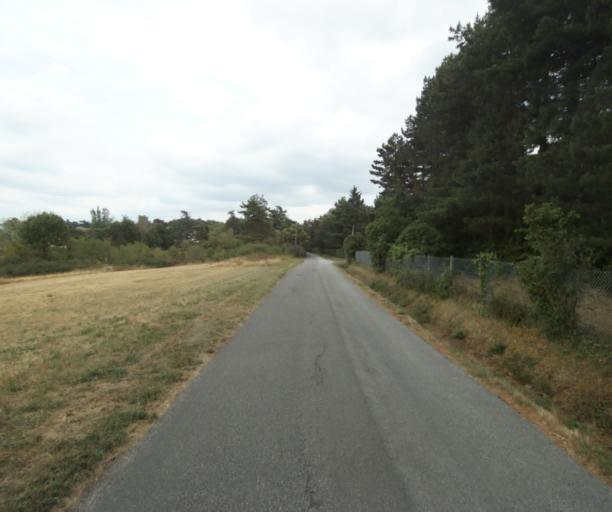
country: FR
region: Midi-Pyrenees
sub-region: Departement de la Haute-Garonne
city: Revel
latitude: 43.4410
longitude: 2.0123
